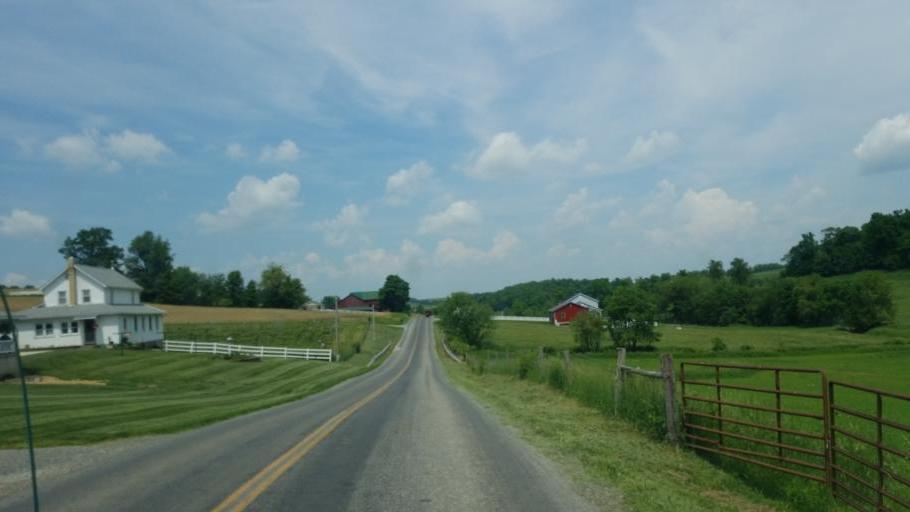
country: US
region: Ohio
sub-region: Holmes County
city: Millersburg
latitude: 40.4920
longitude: -81.7886
